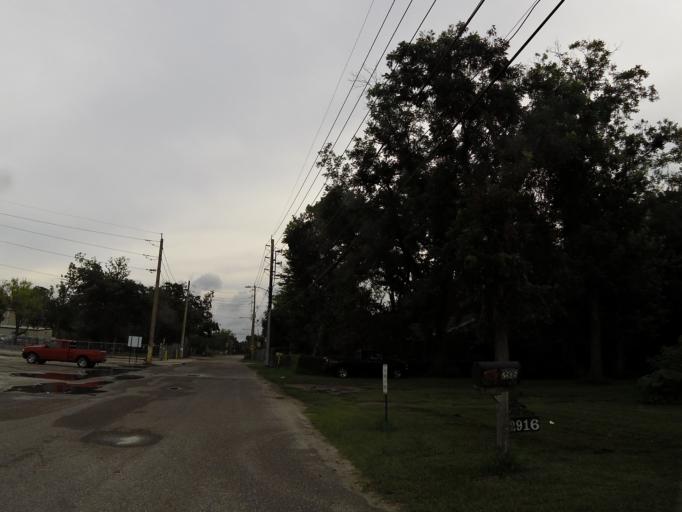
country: US
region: Florida
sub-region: Duval County
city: Jacksonville
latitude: 30.3555
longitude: -81.7163
